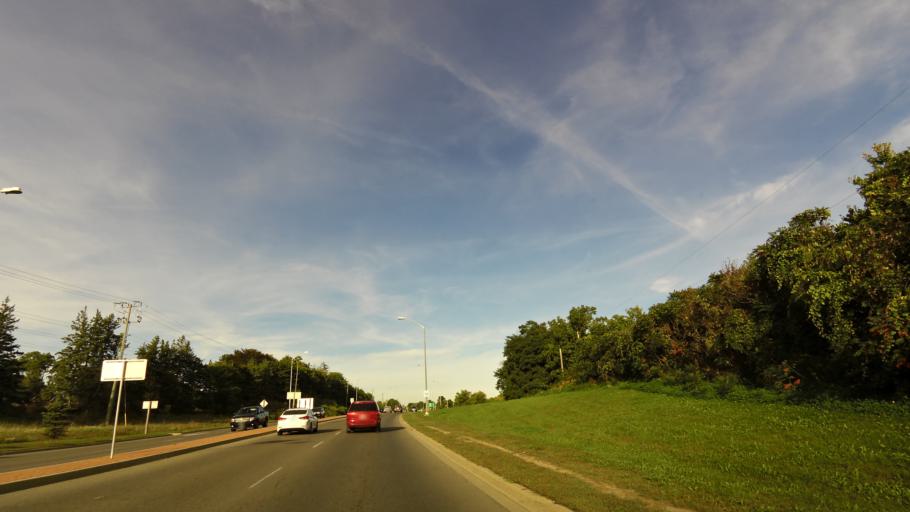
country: CA
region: Ontario
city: Ancaster
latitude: 43.2016
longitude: -80.0129
